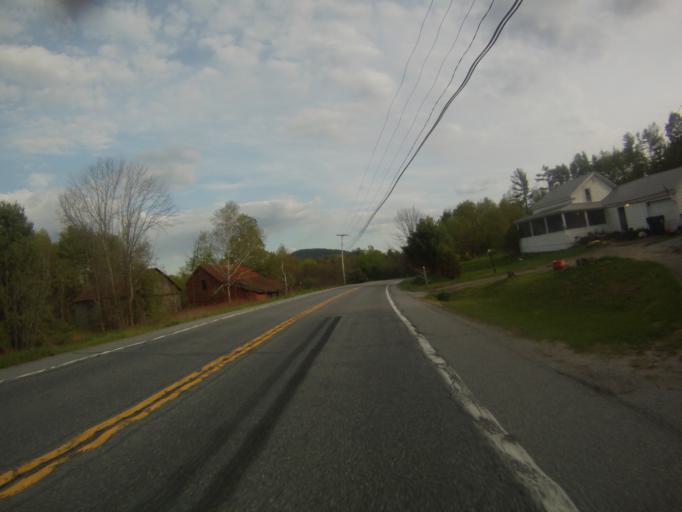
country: US
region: New York
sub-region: Warren County
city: Warrensburg
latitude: 43.6494
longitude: -73.9501
